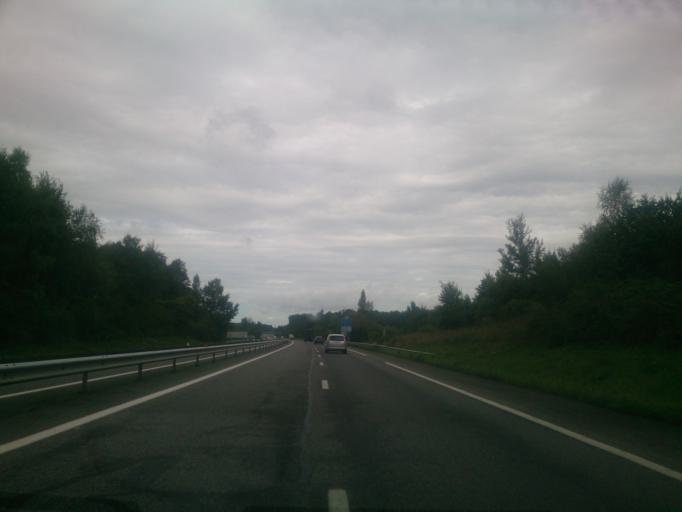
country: FR
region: Midi-Pyrenees
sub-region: Departement de la Haute-Garonne
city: Montrejeau
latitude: 43.0991
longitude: 0.4914
